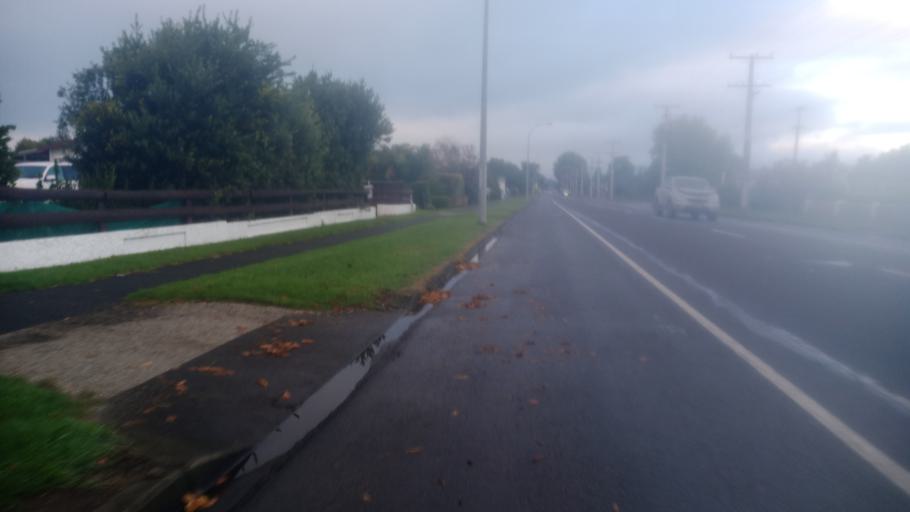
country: NZ
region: Gisborne
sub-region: Gisborne District
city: Gisborne
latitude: -38.6532
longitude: 177.9974
